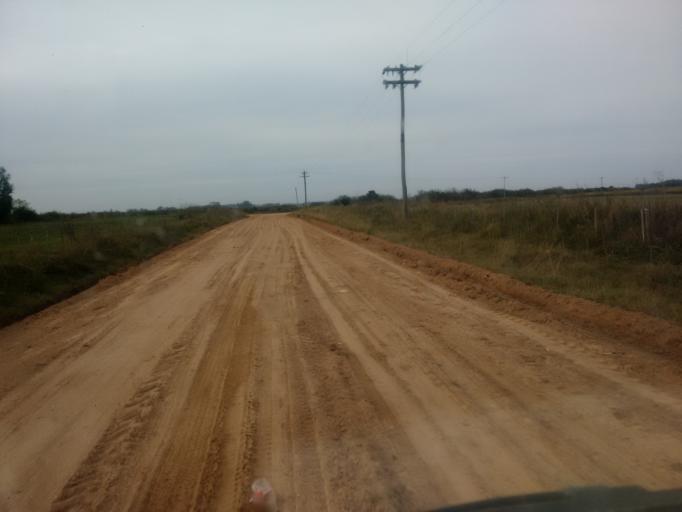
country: BR
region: Rio Grande do Sul
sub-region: Camaqua
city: Camaqua
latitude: -31.1266
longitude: -51.7679
